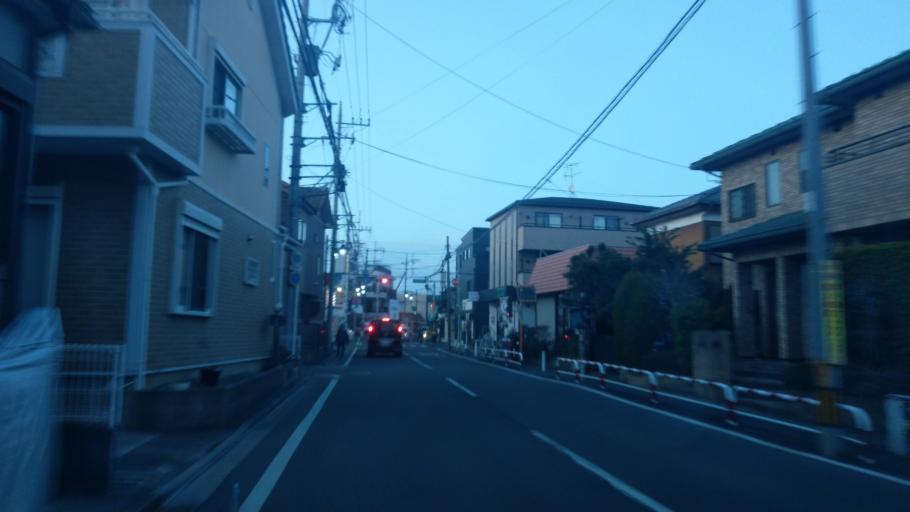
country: JP
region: Saitama
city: Yono
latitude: 35.8786
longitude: 139.6042
